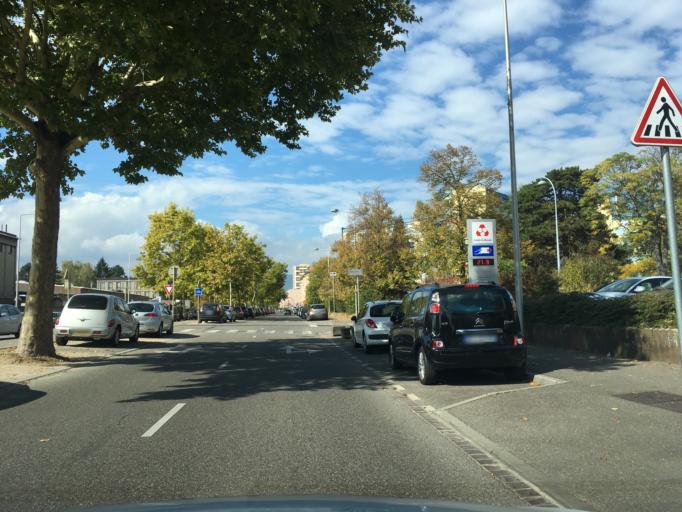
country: FR
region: Alsace
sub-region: Departement du Haut-Rhin
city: Colmar
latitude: 48.0761
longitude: 7.3408
